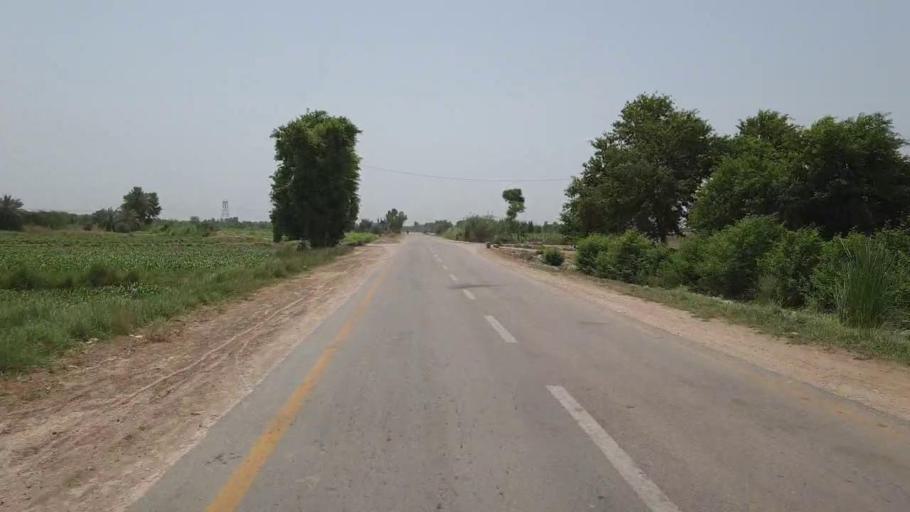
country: PK
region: Sindh
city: Moro
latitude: 26.6095
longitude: 68.0438
